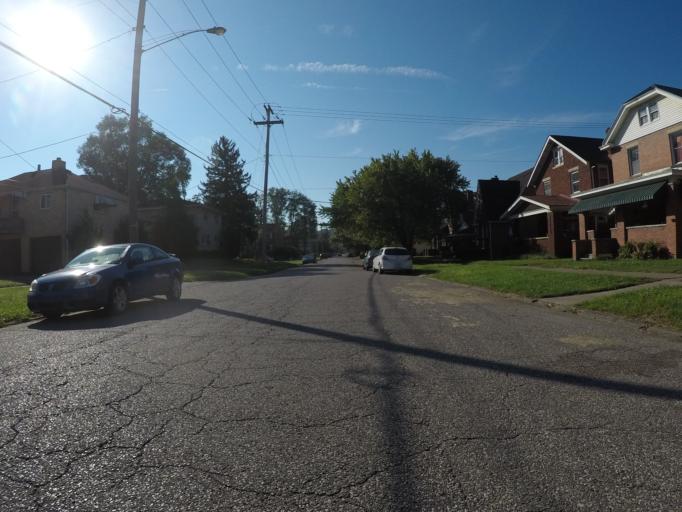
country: US
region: West Virginia
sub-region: Cabell County
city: Huntington
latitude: 38.4129
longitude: -82.4362
